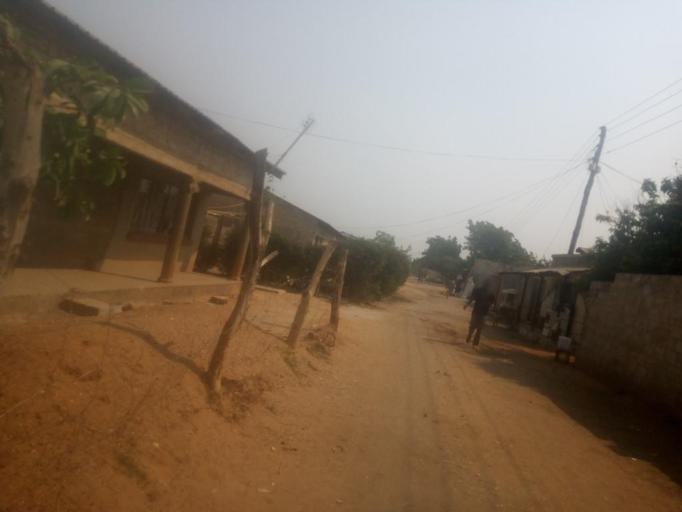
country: ZM
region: Lusaka
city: Lusaka
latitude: -15.3990
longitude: 28.3813
